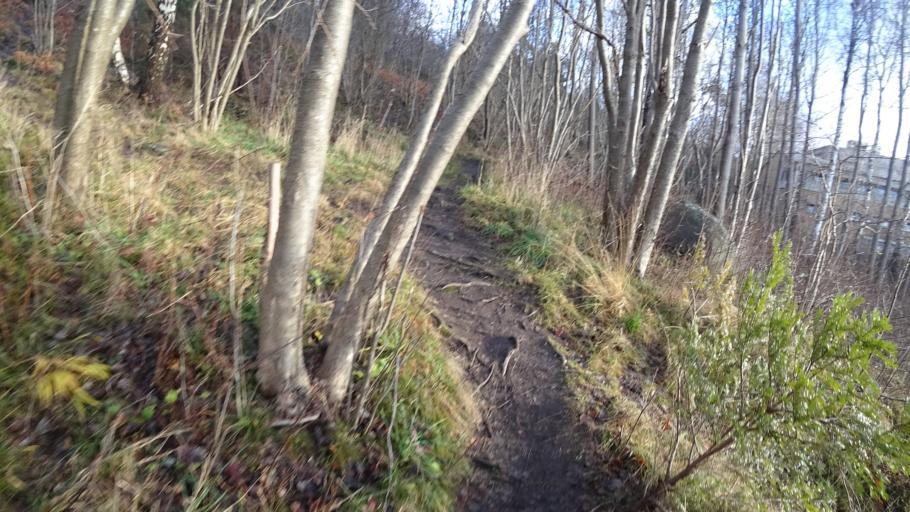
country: SE
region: Vaestra Goetaland
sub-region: Goteborg
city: Majorna
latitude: 57.6665
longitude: 11.9422
